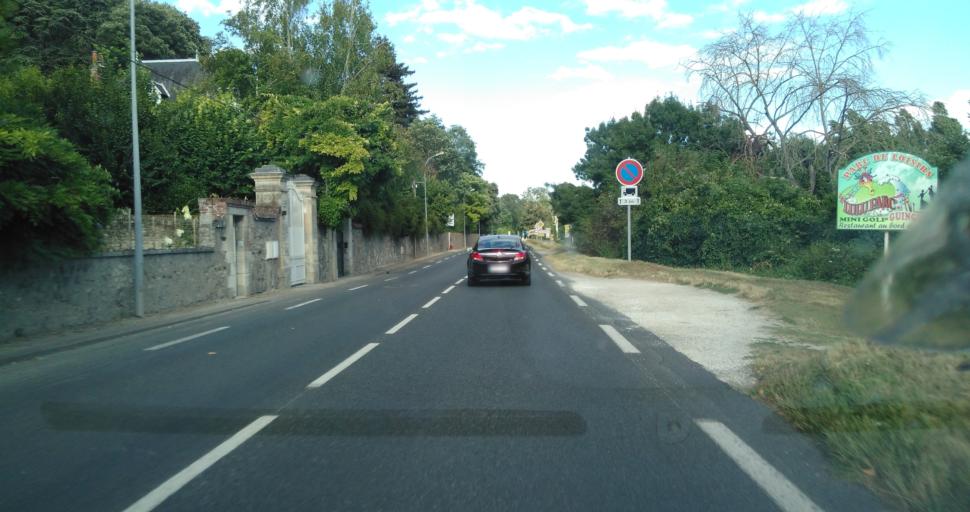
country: FR
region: Centre
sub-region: Departement d'Indre-et-Loire
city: Rochecorbon
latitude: 47.4066
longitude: 0.7417
